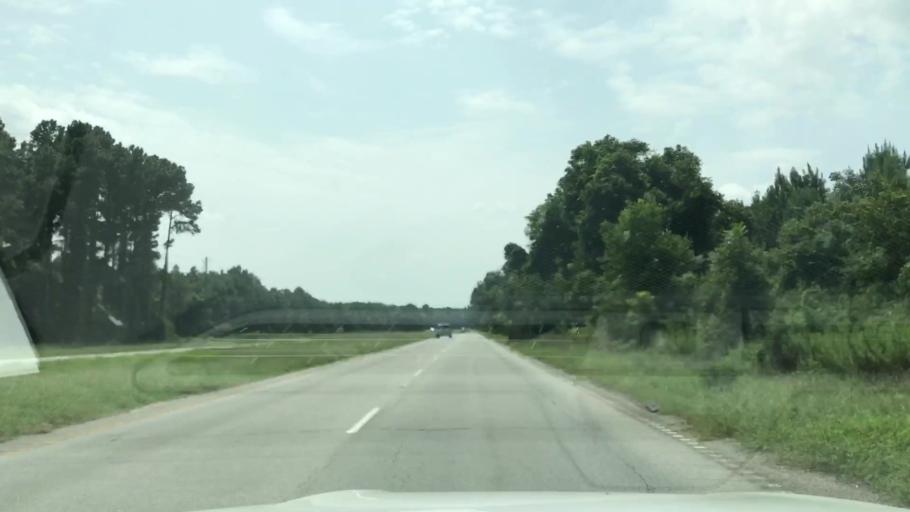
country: US
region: South Carolina
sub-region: Charleston County
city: Awendaw
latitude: 33.0591
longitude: -79.5412
